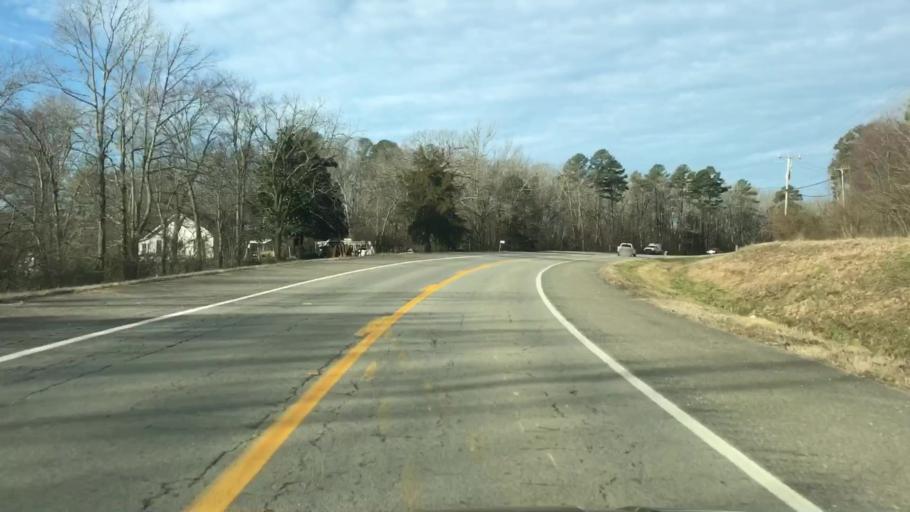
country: US
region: Arkansas
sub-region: Montgomery County
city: Mount Ida
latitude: 34.5392
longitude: -93.6019
